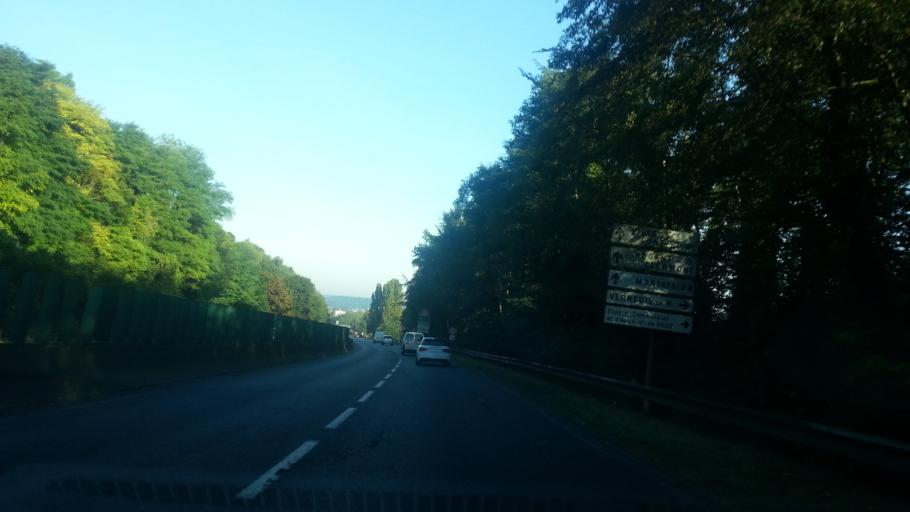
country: FR
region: Picardie
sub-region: Departement de l'Oise
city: Creil
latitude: 49.2600
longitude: 2.4913
